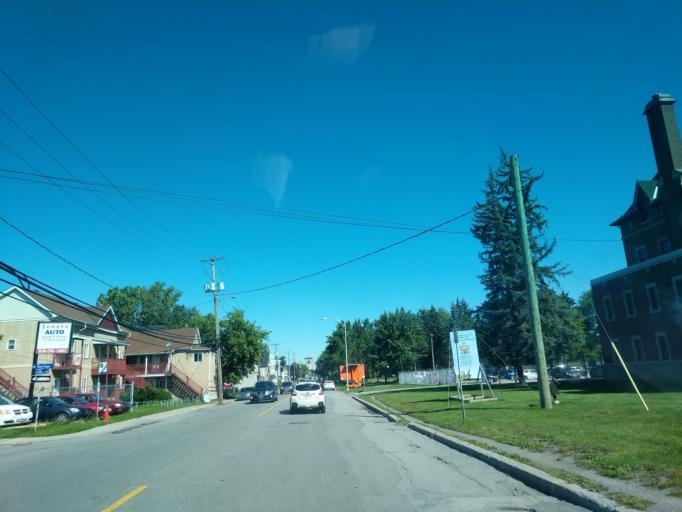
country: CA
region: Ontario
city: Ottawa
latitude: 45.4243
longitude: -75.7335
